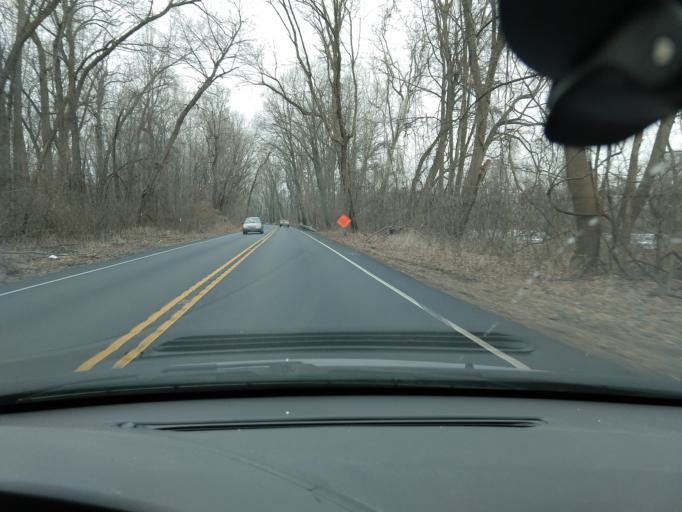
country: US
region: Pennsylvania
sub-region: Montgomery County
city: Stowe
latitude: 40.2391
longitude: -75.6945
